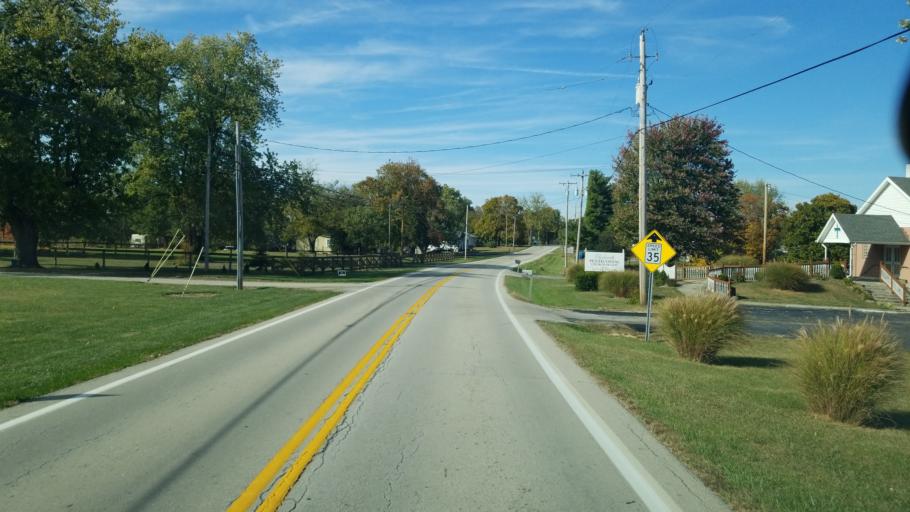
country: US
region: Ohio
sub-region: Clinton County
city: Blanchester
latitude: 39.3949
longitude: -83.9750
